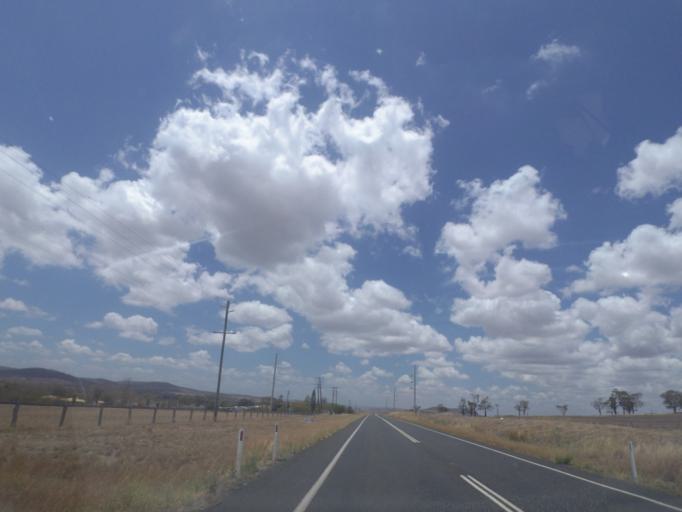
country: AU
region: Queensland
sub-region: Toowoomba
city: Top Camp
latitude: -27.7483
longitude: 151.9306
